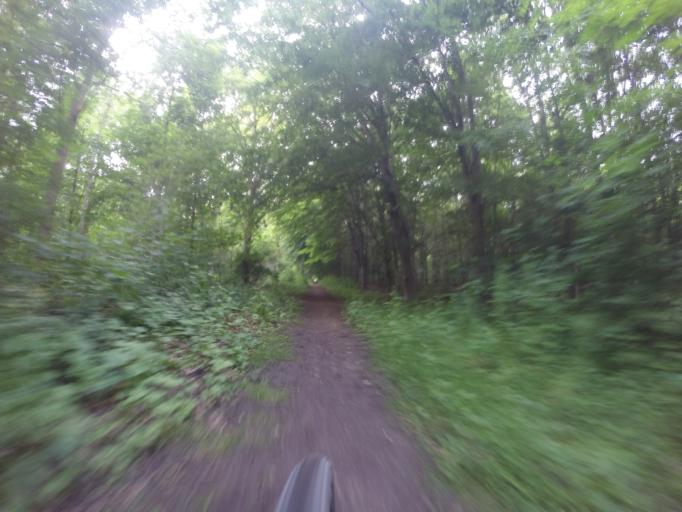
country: DK
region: Capital Region
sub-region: Albertslund Kommune
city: Albertslund
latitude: 55.6937
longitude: 12.3273
